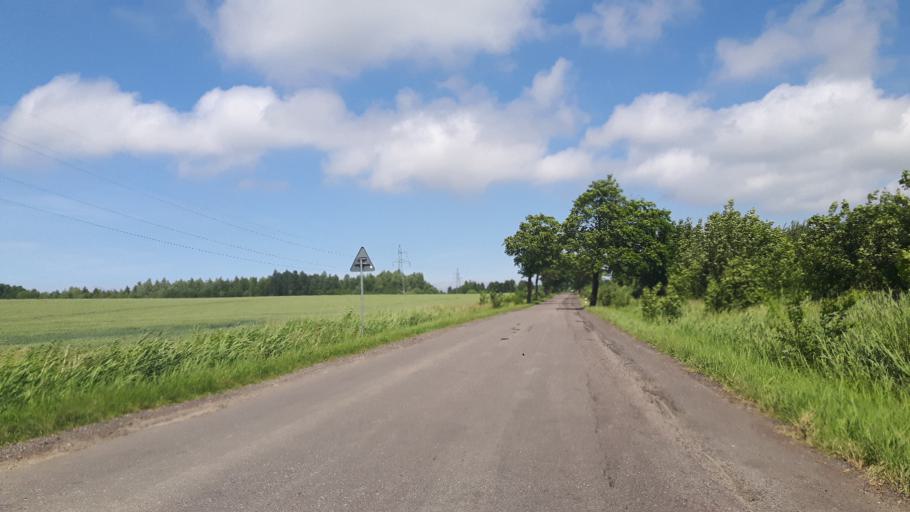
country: PL
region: Pomeranian Voivodeship
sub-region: Powiat slupski
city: Ustka
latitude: 54.5565
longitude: 16.8404
